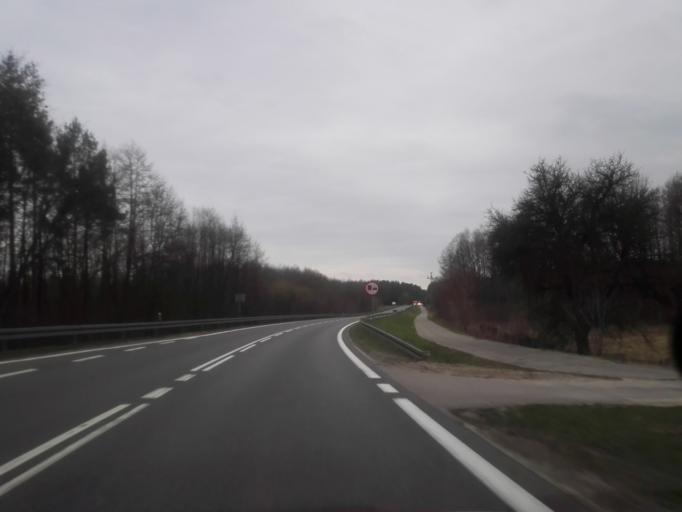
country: PL
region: Podlasie
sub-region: Powiat grajewski
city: Rajgrod
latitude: 53.7074
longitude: 22.6697
